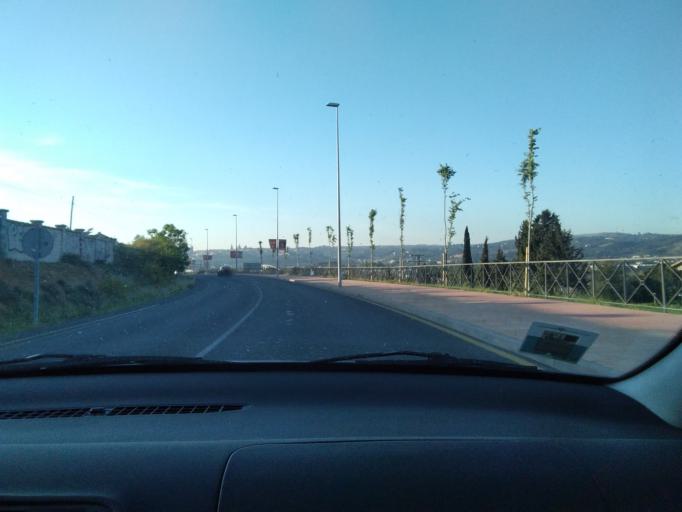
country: ES
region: Castille-La Mancha
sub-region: Province of Toledo
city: Toledo
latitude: 39.8821
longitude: -4.0523
